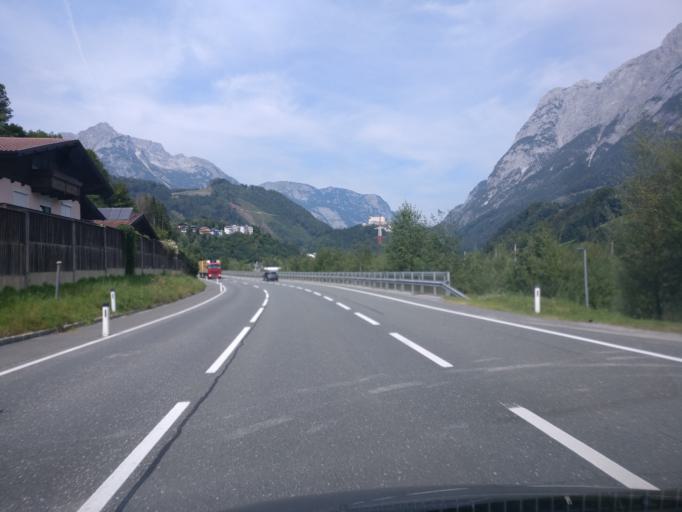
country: AT
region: Salzburg
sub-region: Politischer Bezirk Sankt Johann im Pongau
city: Pfarrwerfen
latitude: 47.4668
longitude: 13.1968
